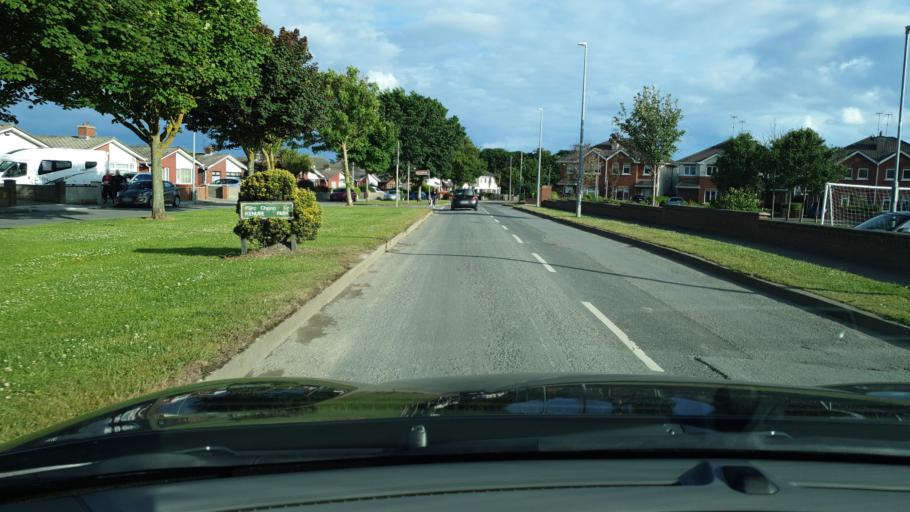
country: IE
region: Leinster
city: An Ros
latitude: 53.5283
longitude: -6.0986
